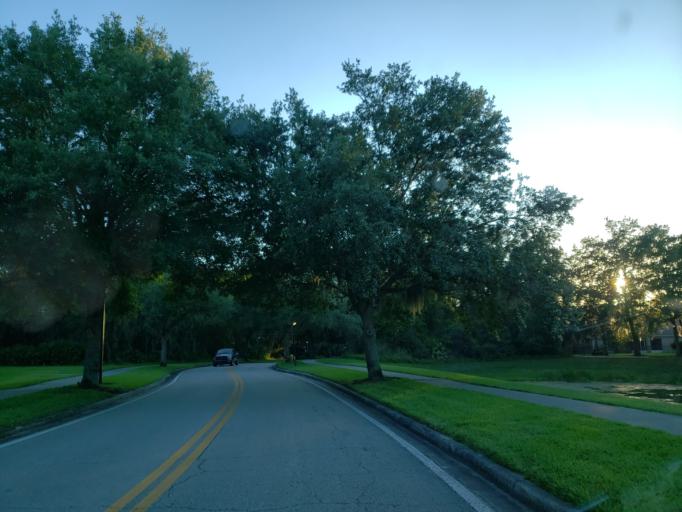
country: US
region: Florida
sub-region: Hillsborough County
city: Boyette
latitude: 27.8381
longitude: -82.2306
